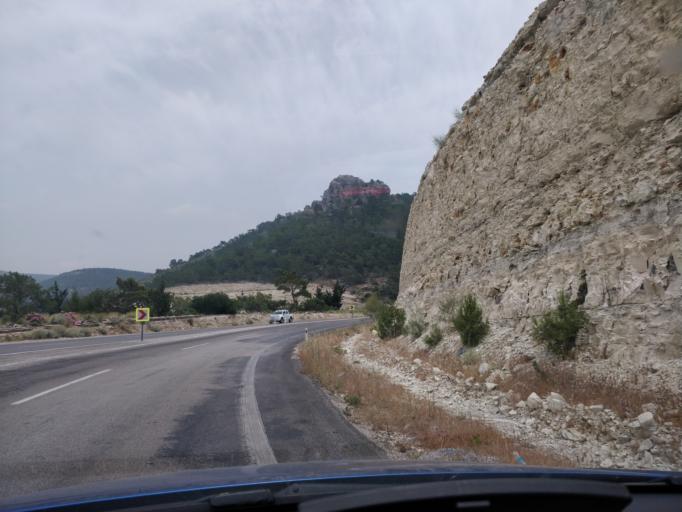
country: TR
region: Mersin
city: Tasucu
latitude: 36.3974
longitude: 33.8528
